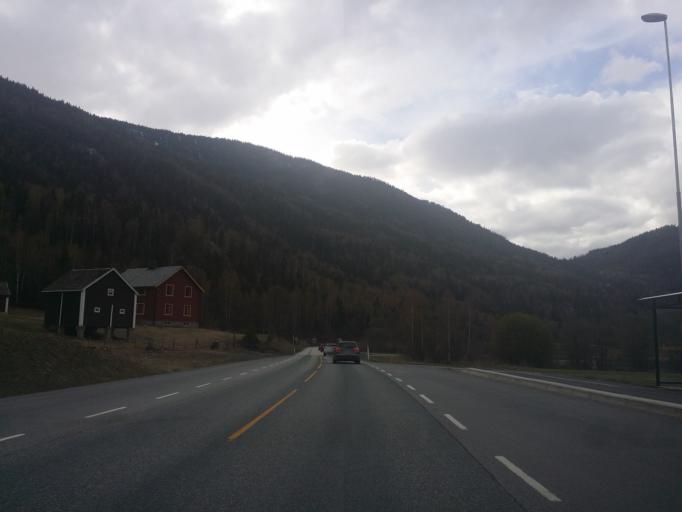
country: NO
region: Buskerud
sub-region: Nes
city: Nesbyen
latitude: 60.4878
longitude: 9.1889
